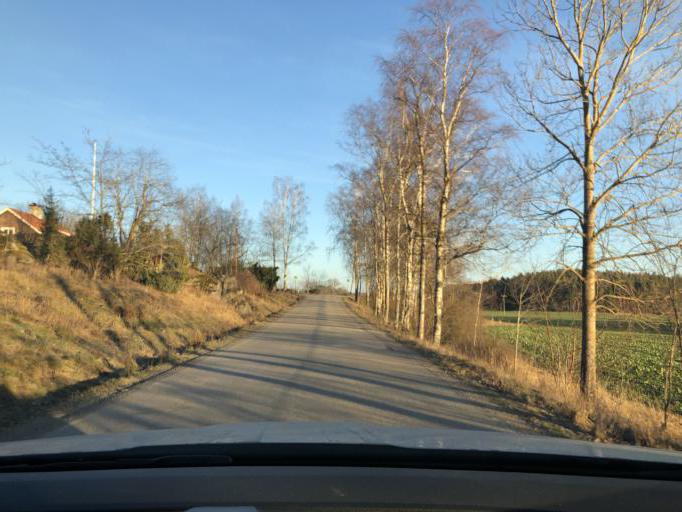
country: SE
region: Soedermanland
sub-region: Eskilstuna Kommun
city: Arla
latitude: 59.4184
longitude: 16.6660
